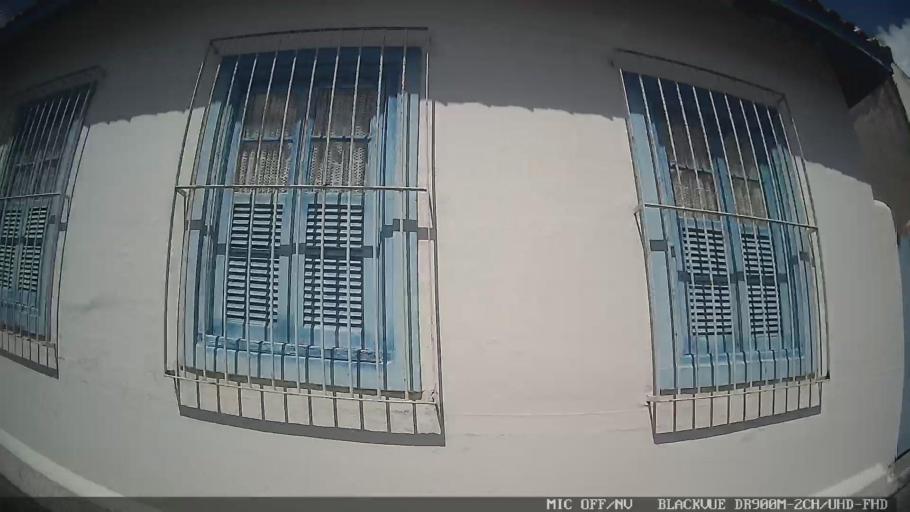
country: BR
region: Sao Paulo
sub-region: Sao Sebastiao
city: Sao Sebastiao
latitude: -23.7621
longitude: -45.4082
